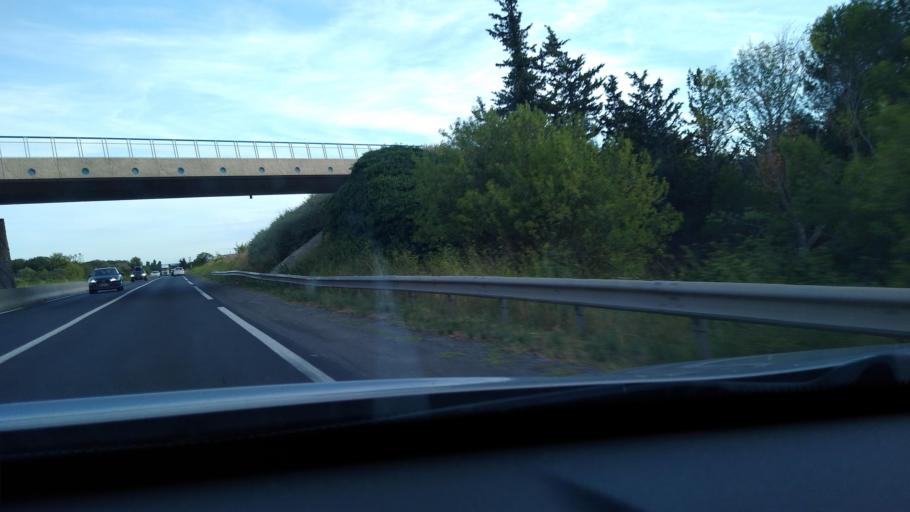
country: FR
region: Languedoc-Roussillon
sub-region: Departement de l'Herault
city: Frontignan
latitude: 43.4302
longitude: 3.7214
